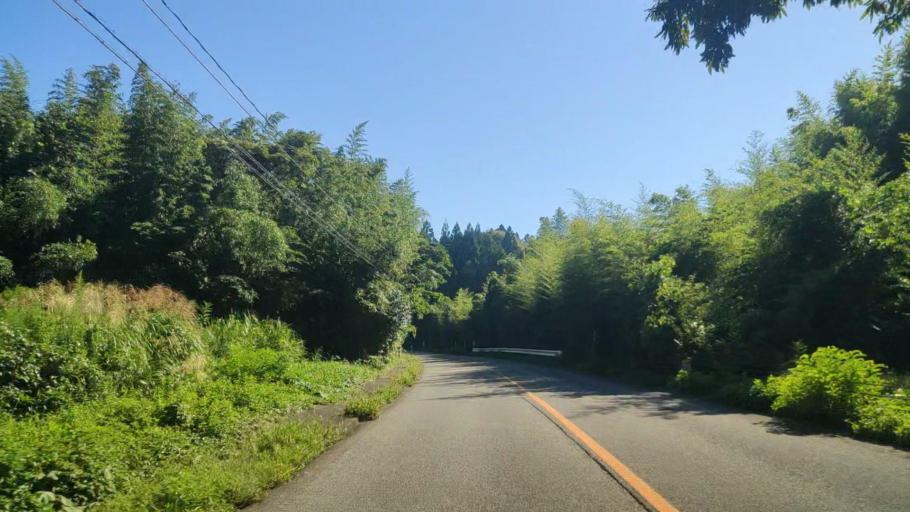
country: JP
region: Ishikawa
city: Nanao
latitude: 37.2620
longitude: 137.0891
